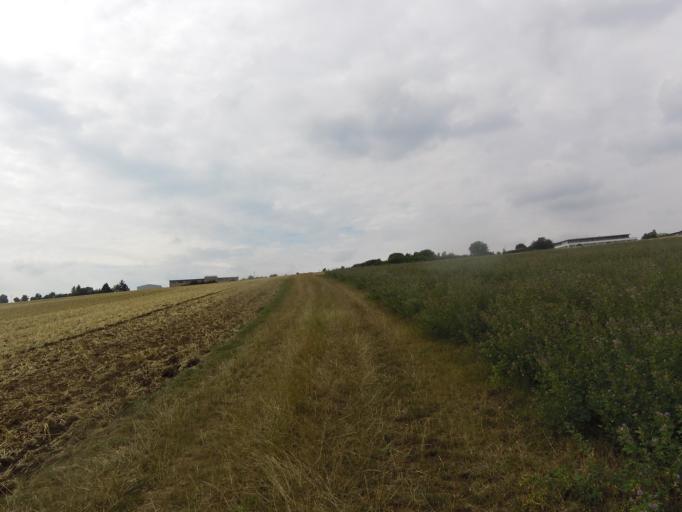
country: DE
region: Bavaria
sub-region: Regierungsbezirk Unterfranken
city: Wuerzburg
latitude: 49.7671
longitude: 9.8711
